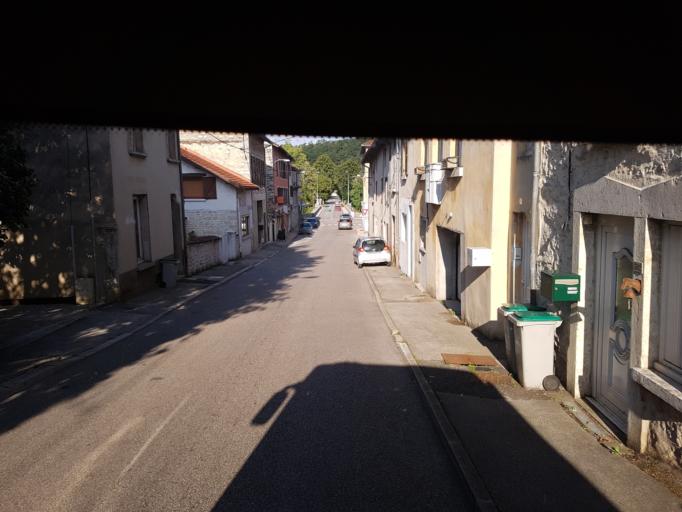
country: FR
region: Rhone-Alpes
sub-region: Departement de l'Ain
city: Neuville-sur-Ain
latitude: 46.0787
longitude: 5.3753
